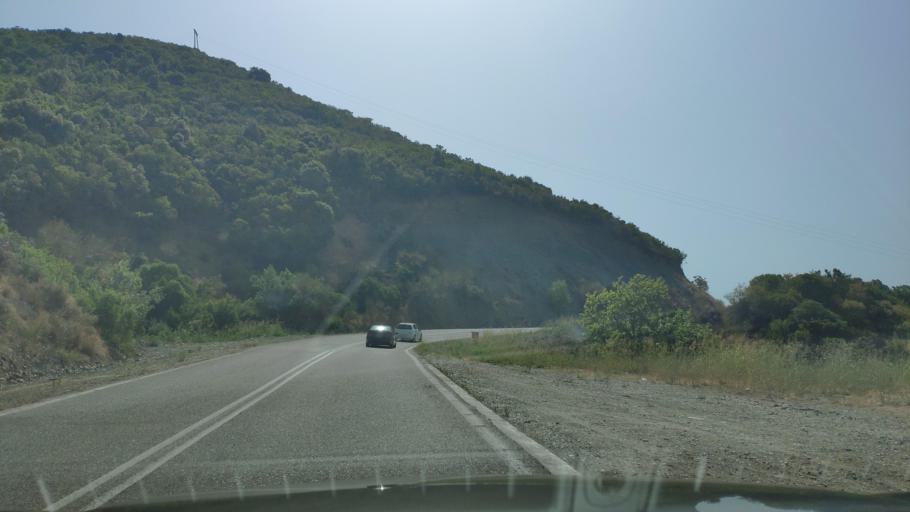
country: GR
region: Epirus
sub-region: Nomos Artas
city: Peta
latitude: 39.1693
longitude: 21.0632
